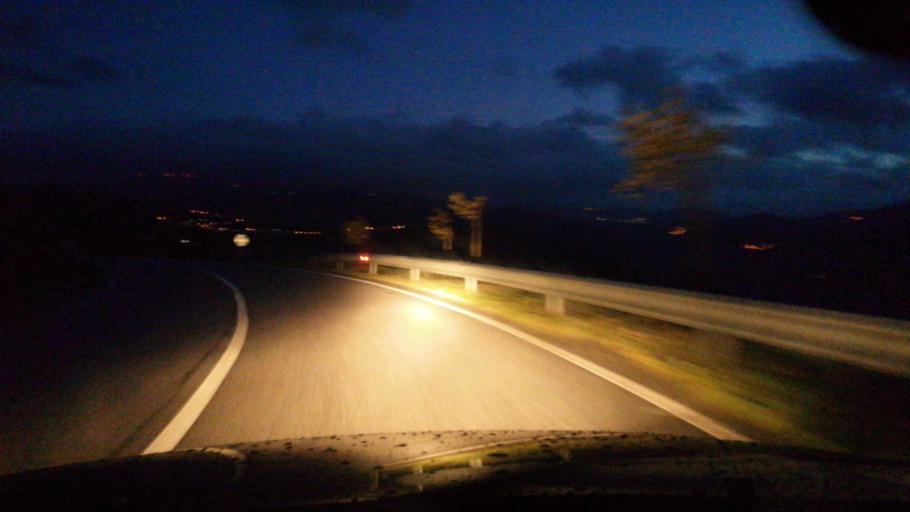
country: PT
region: Viseu
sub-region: Tabuaco
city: Tabuaco
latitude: 41.1218
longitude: -7.5142
